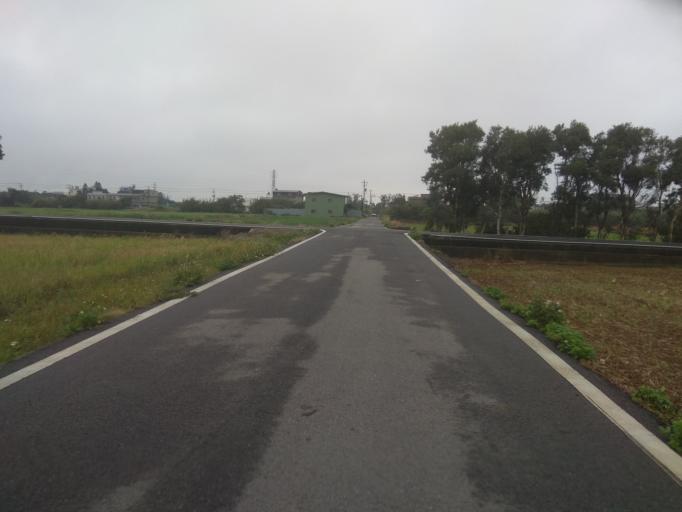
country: TW
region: Taiwan
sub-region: Hsinchu
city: Zhubei
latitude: 24.9907
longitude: 121.0342
